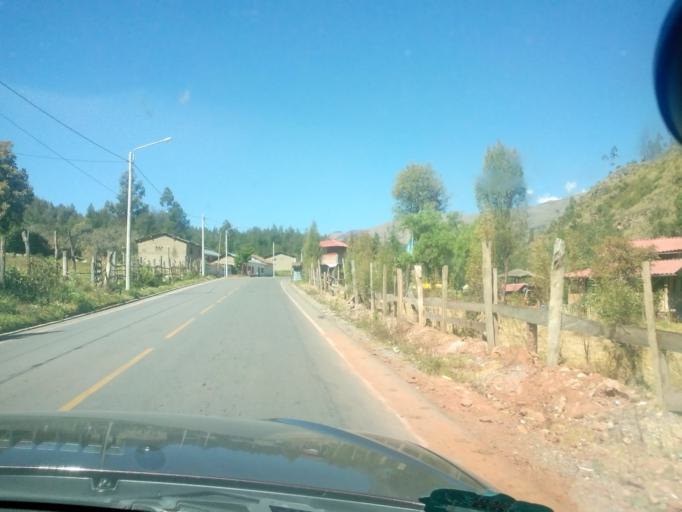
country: PE
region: Apurimac
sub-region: Chincheros
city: Chincheros
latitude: -13.5155
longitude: -73.7049
